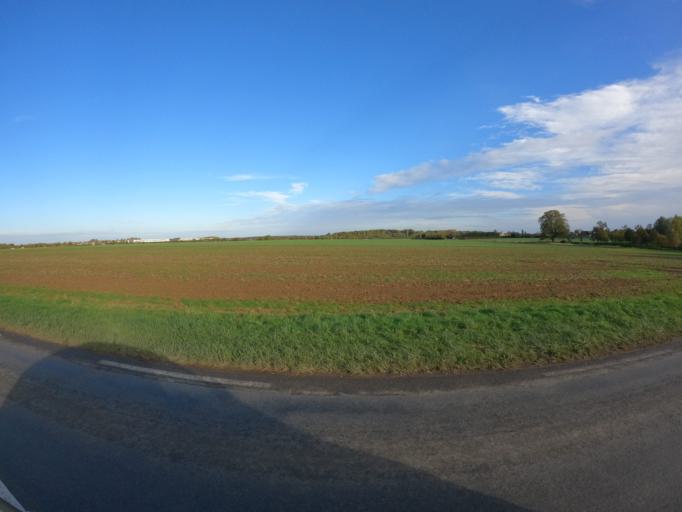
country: FR
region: Ile-de-France
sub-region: Departement de Seine-et-Marne
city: Chanteloup-en-Brie
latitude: 48.8377
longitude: 2.7464
